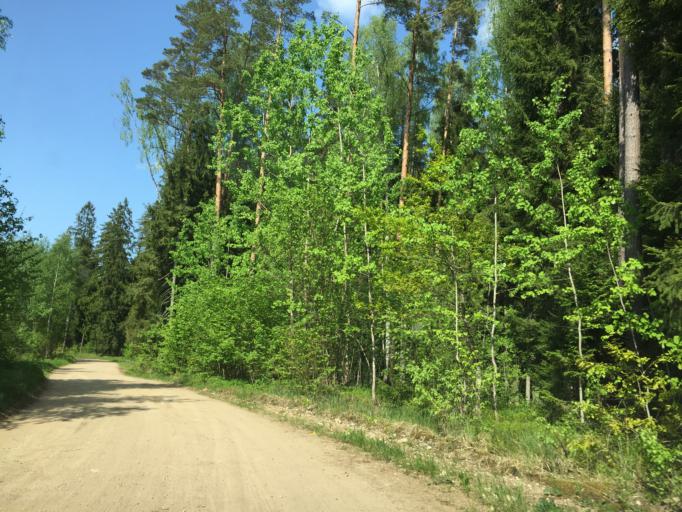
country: LV
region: Baldone
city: Baldone
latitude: 56.8007
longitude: 24.4250
